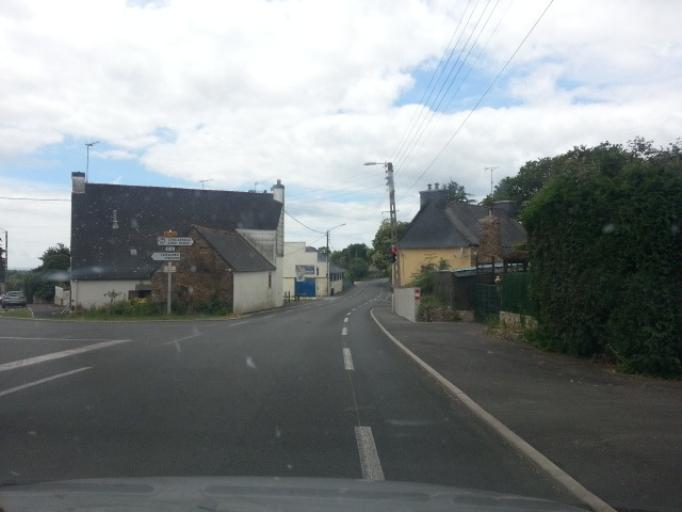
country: FR
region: Brittany
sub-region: Departement du Finistere
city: Melgven
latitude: 47.8799
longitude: -3.8484
